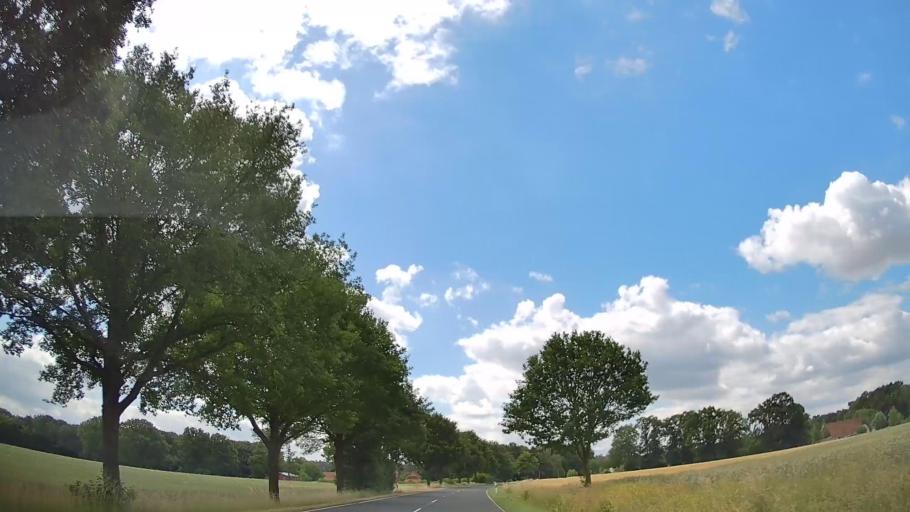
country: DE
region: North Rhine-Westphalia
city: Rahden
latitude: 52.4121
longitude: 8.5215
